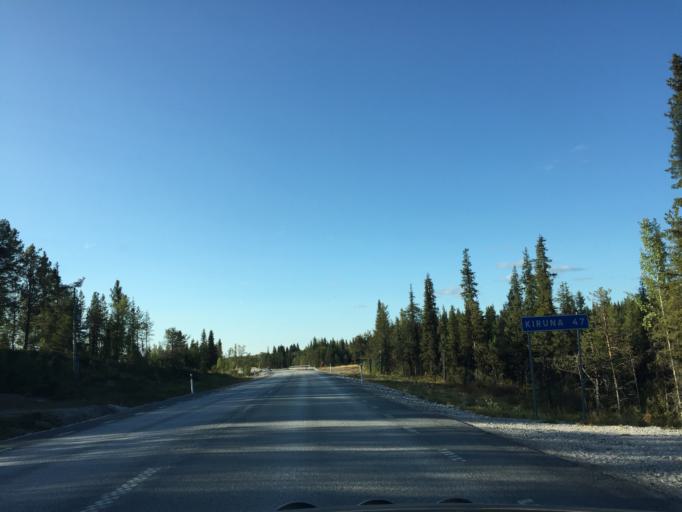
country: SE
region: Norrbotten
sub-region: Gallivare Kommun
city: Malmberget
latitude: 67.6383
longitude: 21.0636
